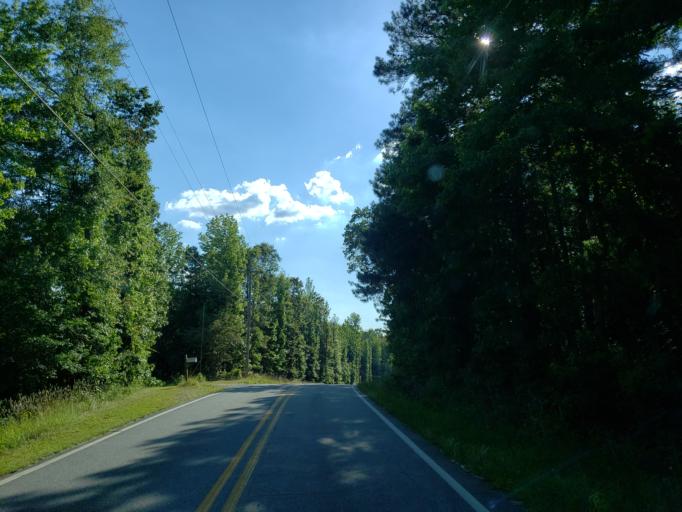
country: US
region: Georgia
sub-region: Carroll County
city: Carrollton
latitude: 33.6499
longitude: -85.0928
